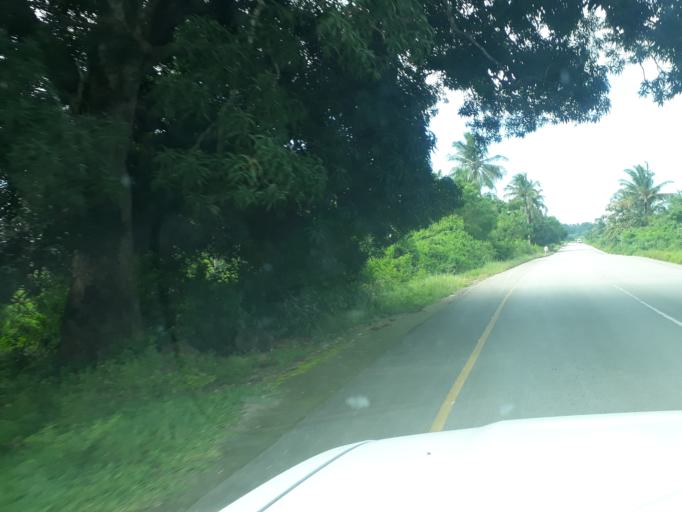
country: TZ
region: Zanzibar North
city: Kijini
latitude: -5.8402
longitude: 39.2845
